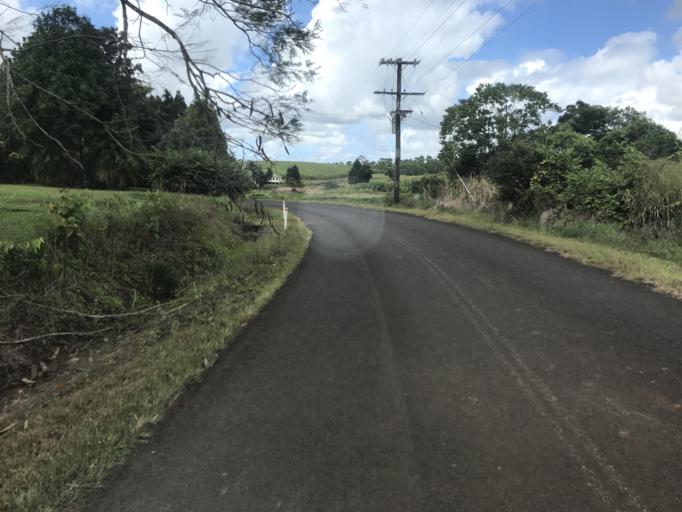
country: AU
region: Queensland
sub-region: Cassowary Coast
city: Innisfail
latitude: -17.5501
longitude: 145.8775
